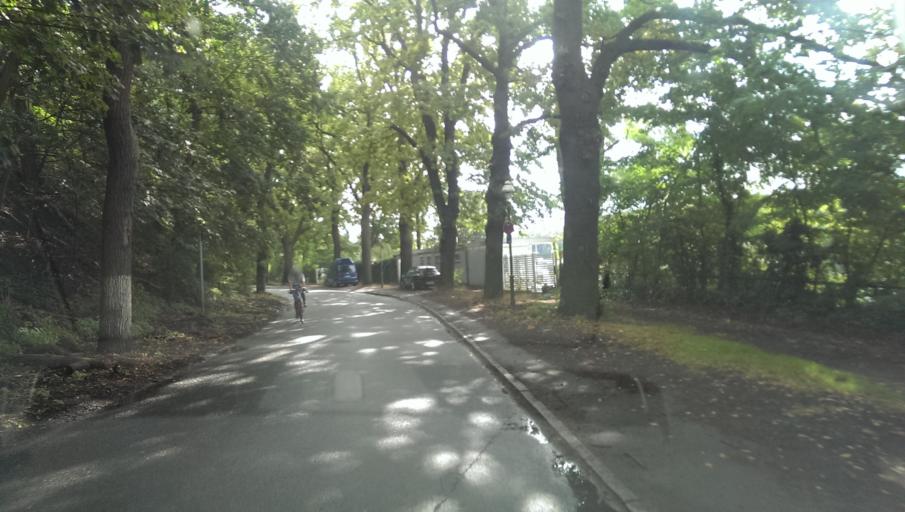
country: DE
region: Berlin
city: Gatow
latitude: 52.5086
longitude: 13.2142
